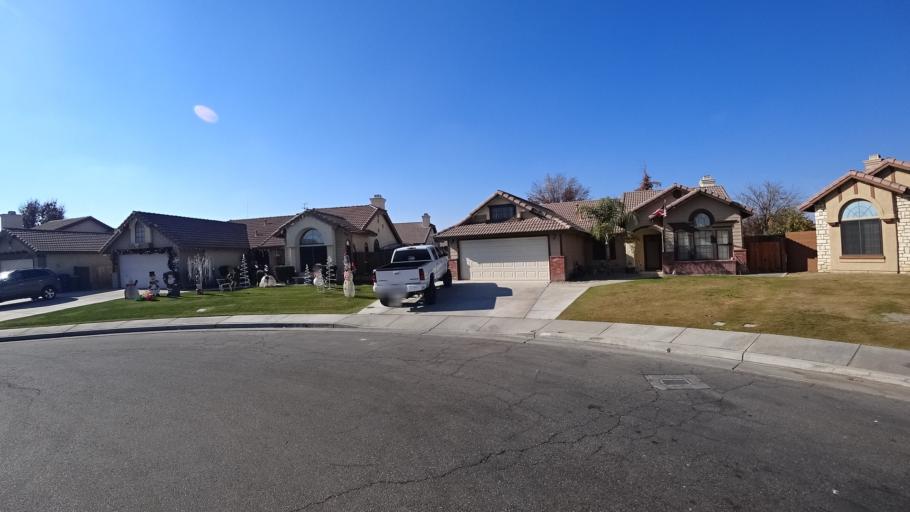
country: US
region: California
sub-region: Kern County
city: Greenfield
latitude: 35.2920
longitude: -119.0531
